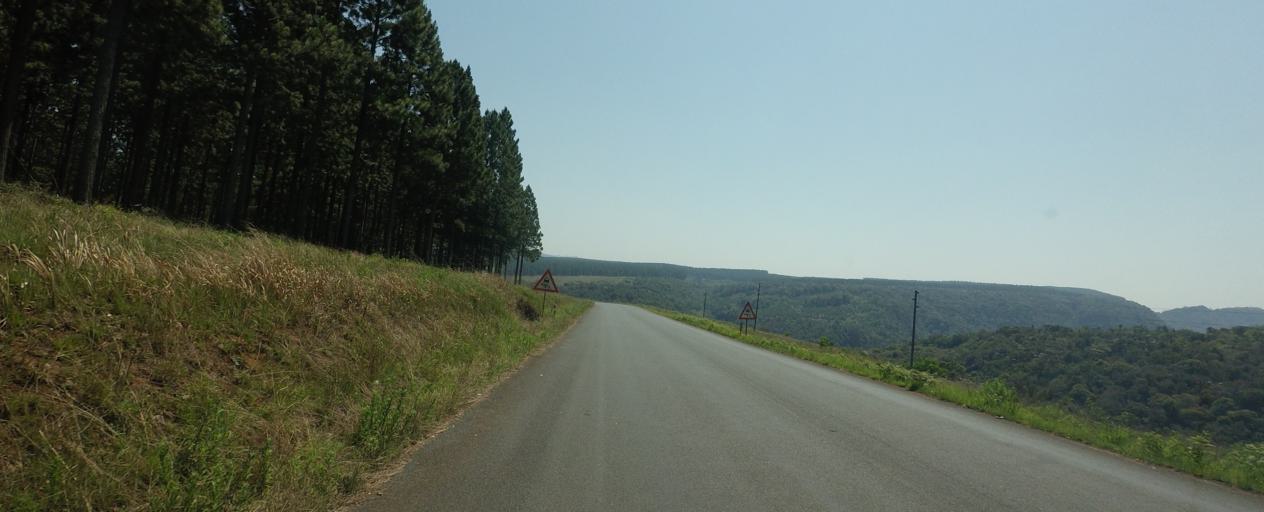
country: ZA
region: Mpumalanga
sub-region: Ehlanzeni District
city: Graksop
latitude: -25.0050
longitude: 30.8227
